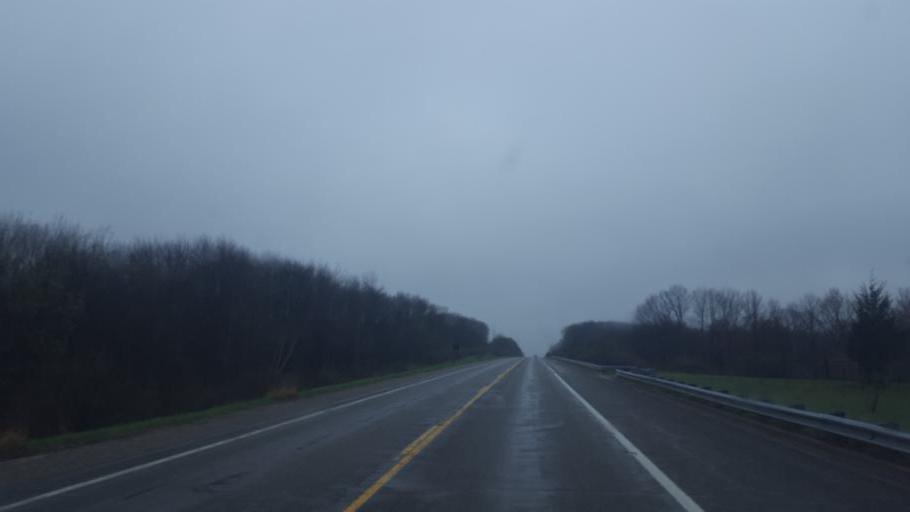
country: US
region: Michigan
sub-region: Isabella County
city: Lake Isabella
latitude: 43.5965
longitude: -84.9657
